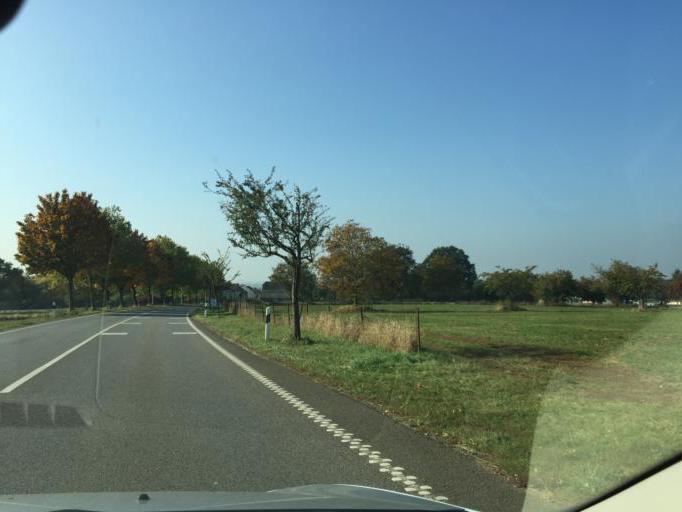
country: LU
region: Grevenmacher
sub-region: Canton de Remich
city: Dalheim
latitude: 49.5370
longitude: 6.2517
